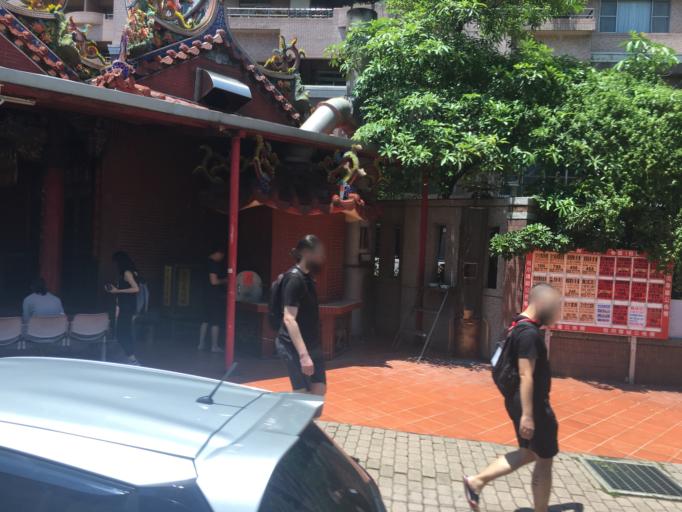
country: TW
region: Taiwan
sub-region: Hsinchu
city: Hsinchu
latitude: 24.7896
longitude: 121.0004
